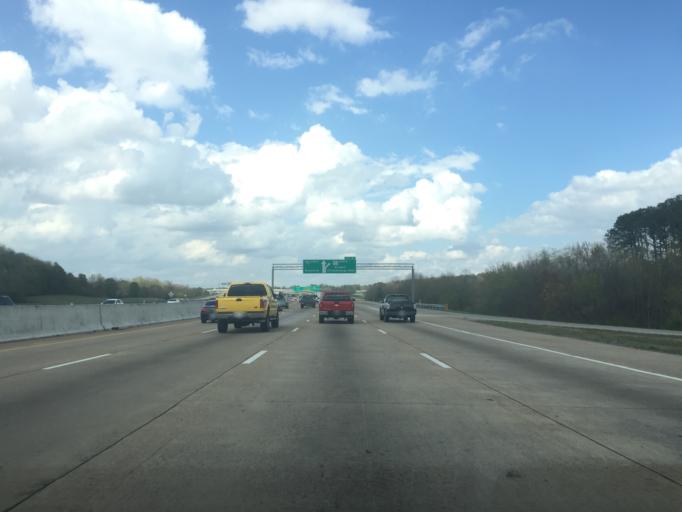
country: US
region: Tennessee
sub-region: Hamilton County
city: East Brainerd
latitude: 35.0200
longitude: -85.1769
